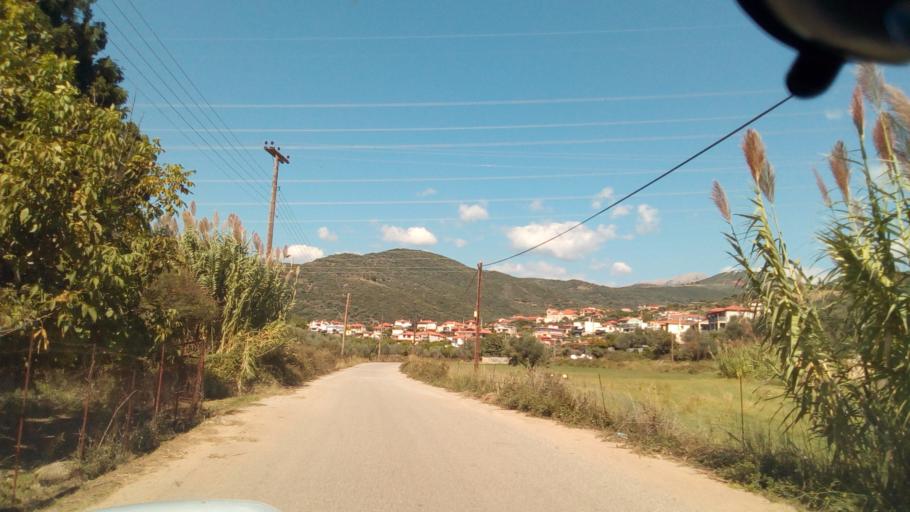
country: GR
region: West Greece
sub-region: Nomos Aitolias kai Akarnanias
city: Nafpaktos
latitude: 38.4115
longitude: 21.8969
